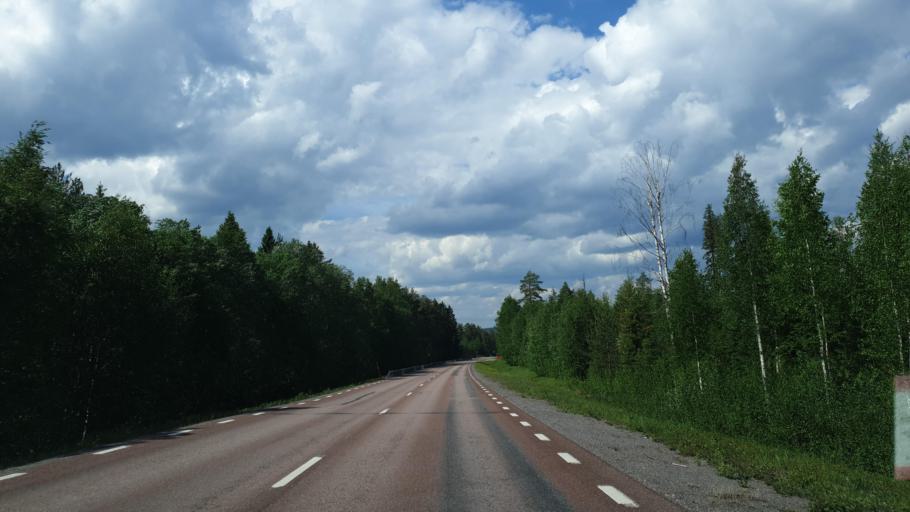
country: SE
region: Norrbotten
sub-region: Alvsbyns Kommun
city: AElvsbyn
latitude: 65.6505
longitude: 21.2374
